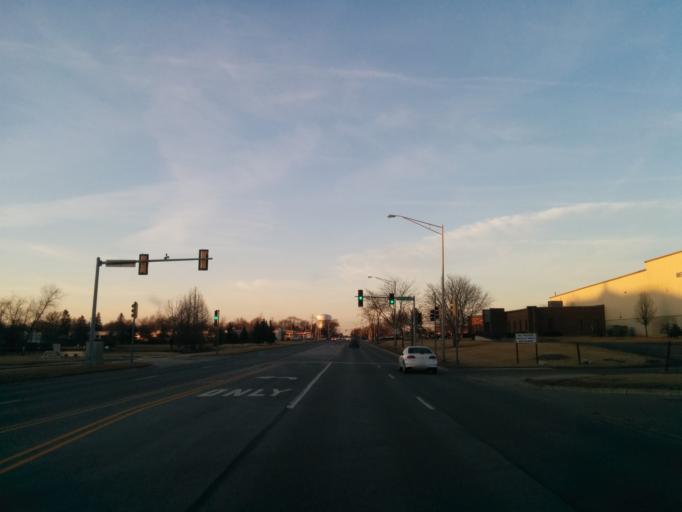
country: US
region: Illinois
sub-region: DuPage County
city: Glendale Heights
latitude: 41.9291
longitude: -88.0421
